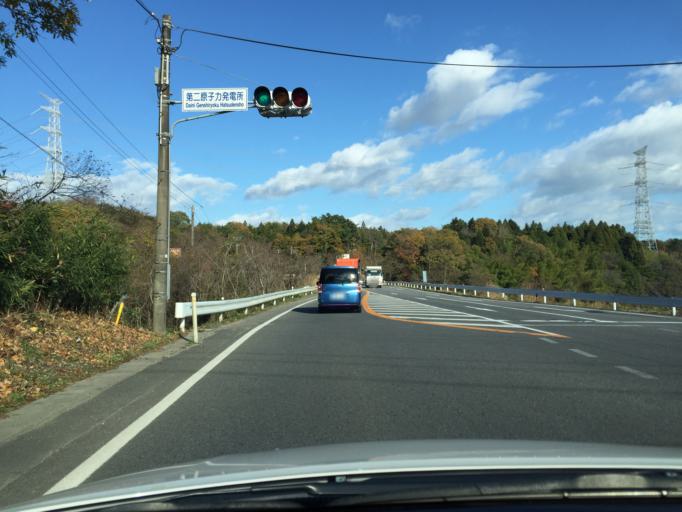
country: JP
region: Fukushima
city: Namie
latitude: 37.3129
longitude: 141.0007
